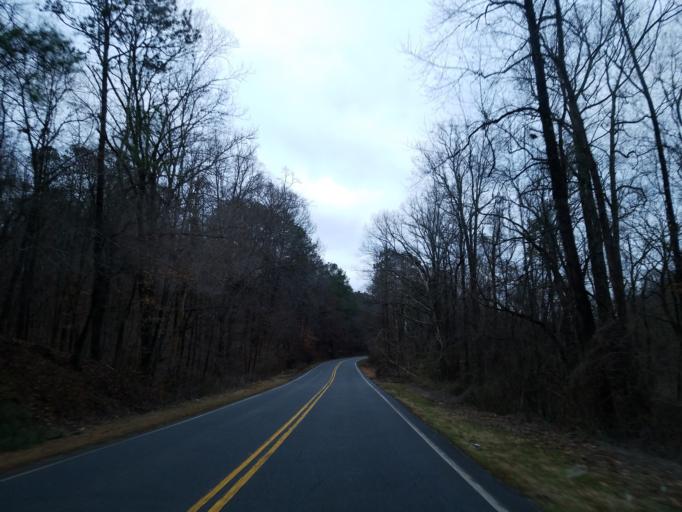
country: US
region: Georgia
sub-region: Bartow County
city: Emerson
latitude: 34.1063
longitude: -84.7439
